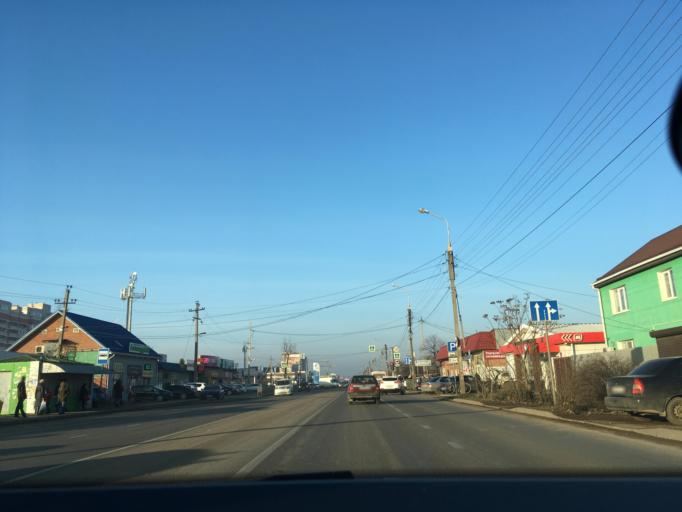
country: RU
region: Krasnodarskiy
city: Krasnodar
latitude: 45.1097
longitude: 39.0124
